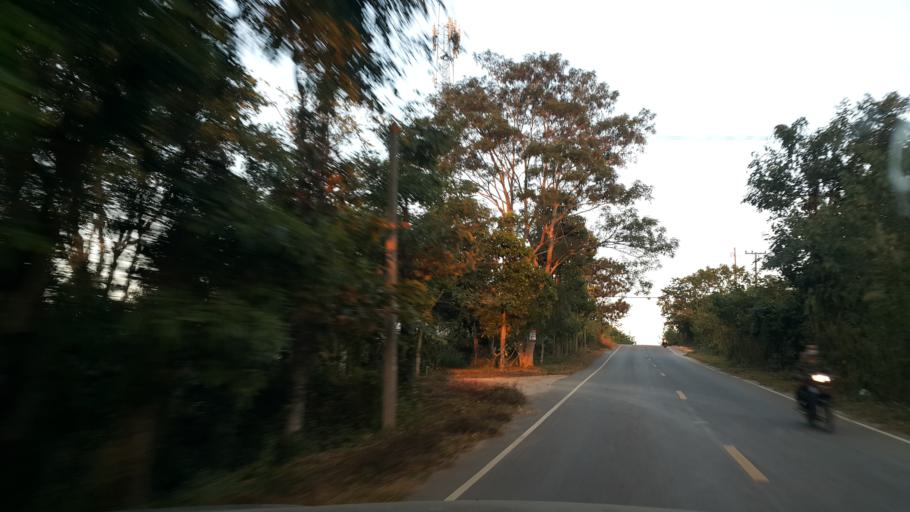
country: TH
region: Phrae
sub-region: Amphoe Wang Chin
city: Wang Chin
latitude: 17.8802
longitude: 99.6222
